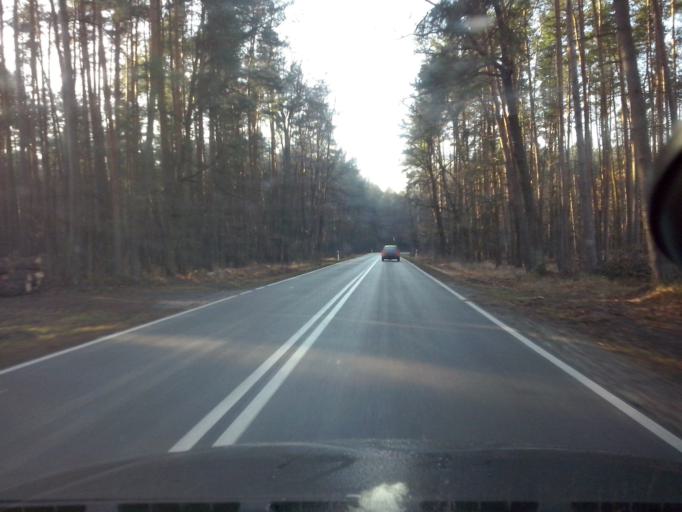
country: PL
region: Subcarpathian Voivodeship
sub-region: Powiat nizanski
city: Bieliny
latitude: 50.3947
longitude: 22.2816
